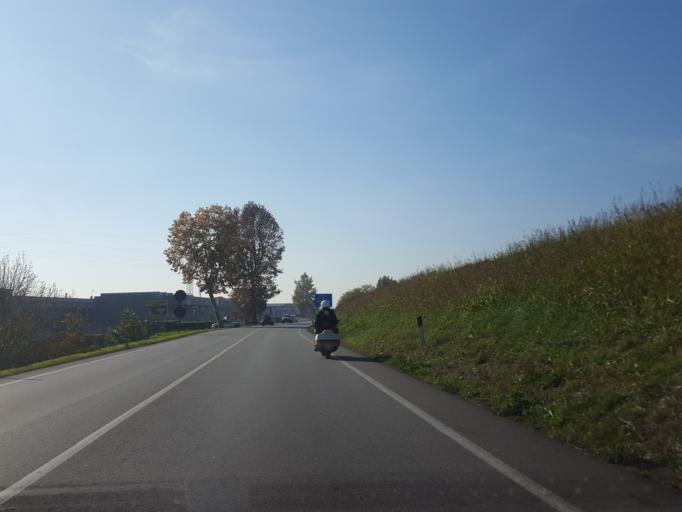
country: IT
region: Veneto
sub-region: Provincia di Vicenza
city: Montebello Vicentino
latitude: 45.4463
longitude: 11.3781
